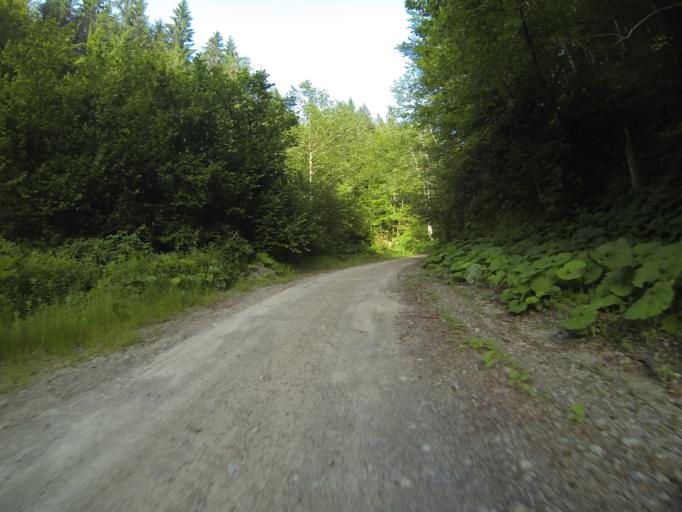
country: RO
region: Valcea
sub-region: Oras Baile Olanesti
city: Baile Olanesti
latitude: 45.2385
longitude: 24.1934
